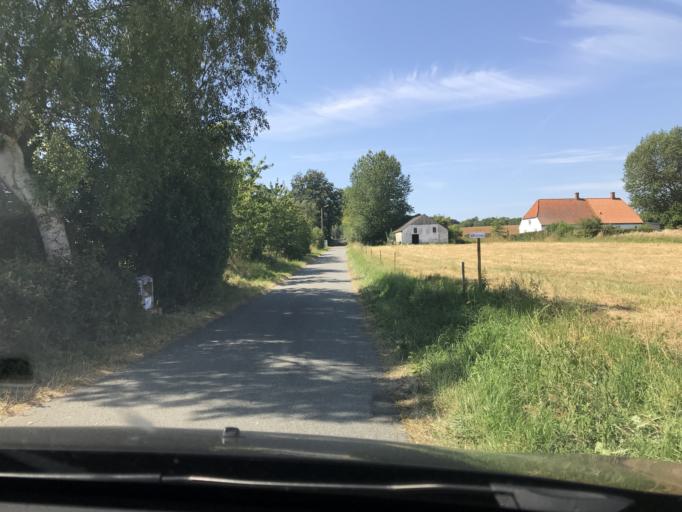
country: DK
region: South Denmark
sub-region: AEro Kommune
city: AEroskobing
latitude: 54.9106
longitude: 10.3224
